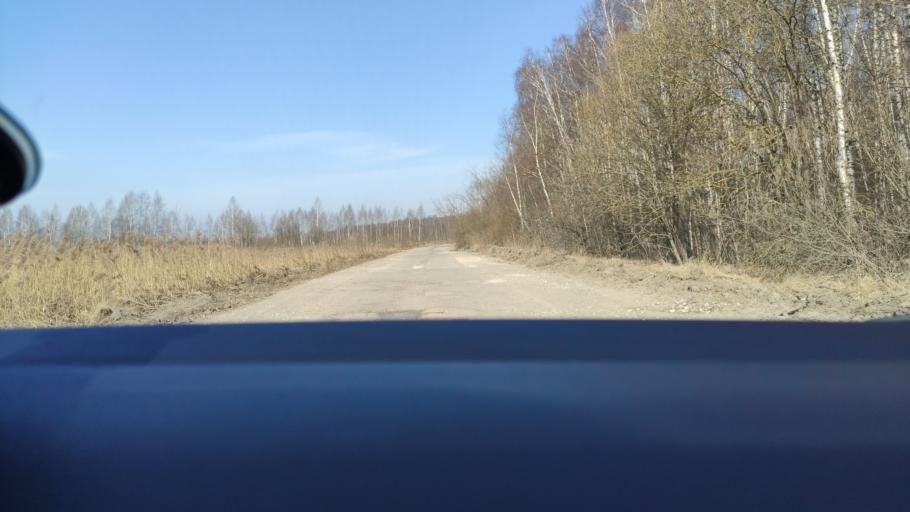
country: RU
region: Moskovskaya
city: Elektrostal'
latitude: 55.7700
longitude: 38.3835
